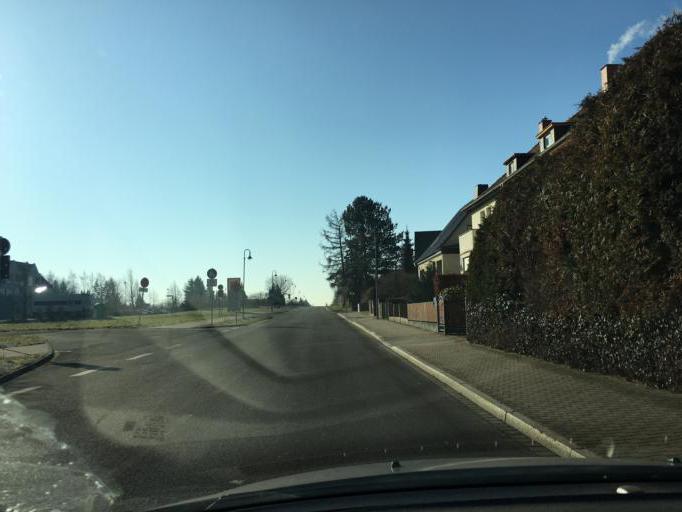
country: DE
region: Saxony
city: Grossposna
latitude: 51.2766
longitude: 12.4694
